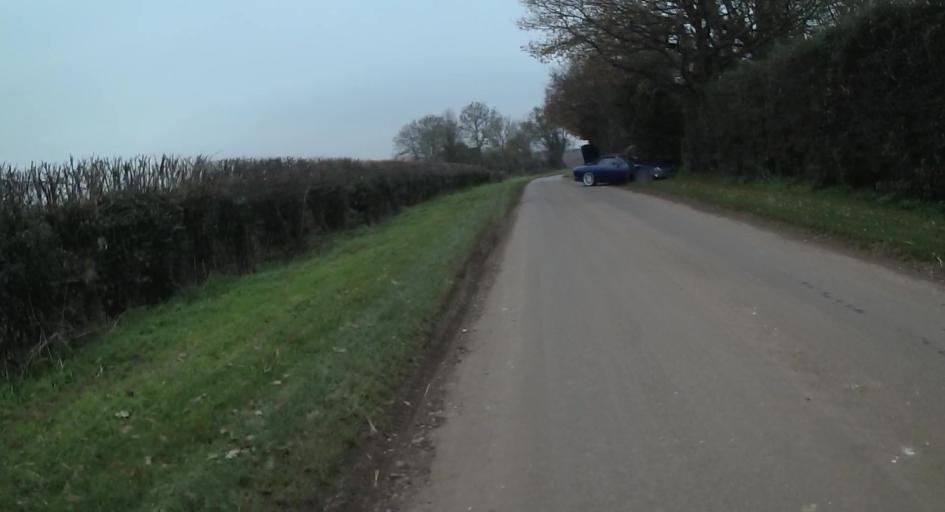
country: GB
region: England
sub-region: Hampshire
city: Kings Worthy
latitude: 51.1031
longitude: -1.2241
